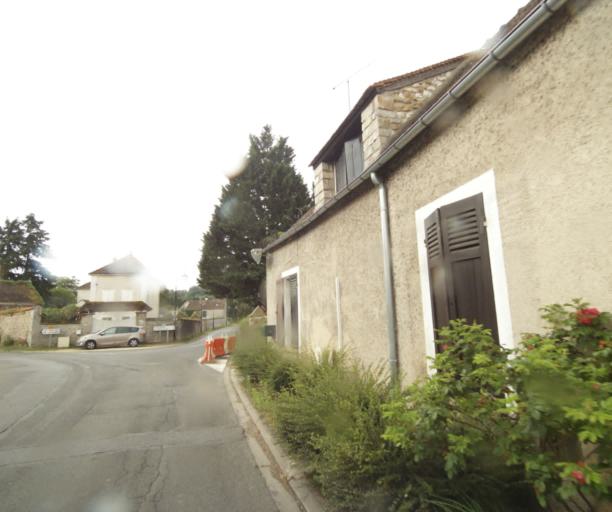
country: FR
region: Ile-de-France
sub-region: Departement de Seine-et-Marne
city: Saint-Sauveur-sur-Ecole
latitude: 48.4936
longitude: 2.5438
